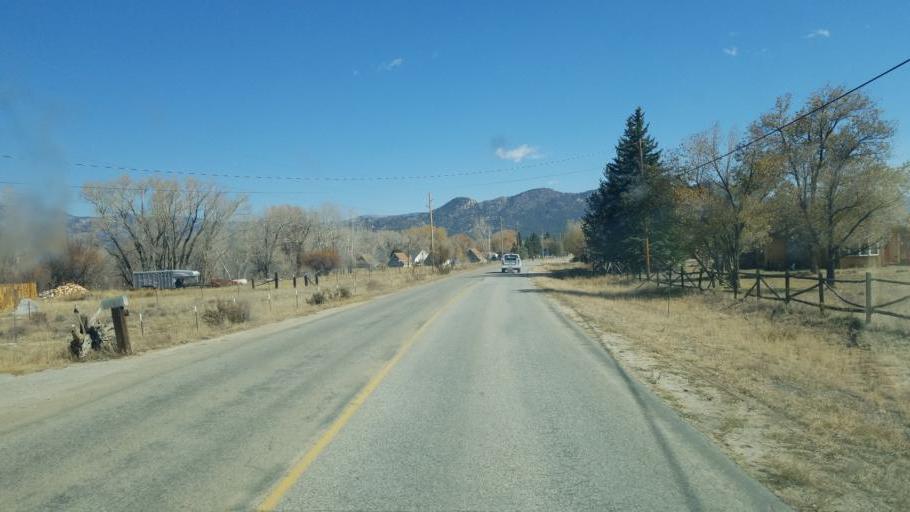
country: US
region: Colorado
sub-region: Chaffee County
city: Buena Vista
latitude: 38.8324
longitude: -106.1673
